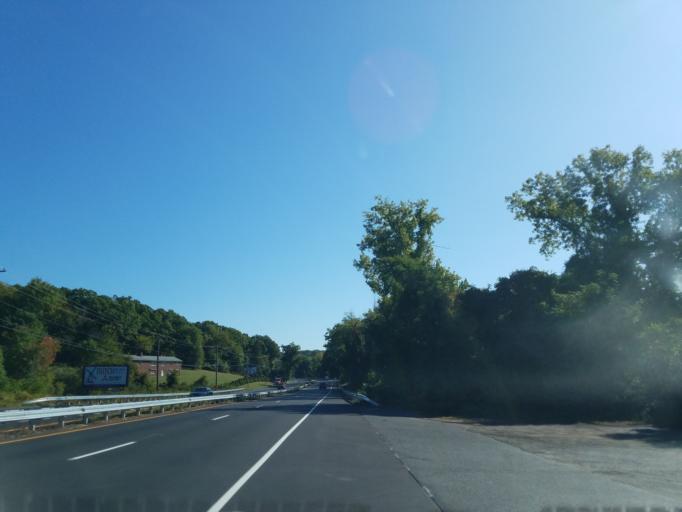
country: US
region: Connecticut
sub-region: Middlesex County
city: Portland
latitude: 41.5692
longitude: -72.6226
